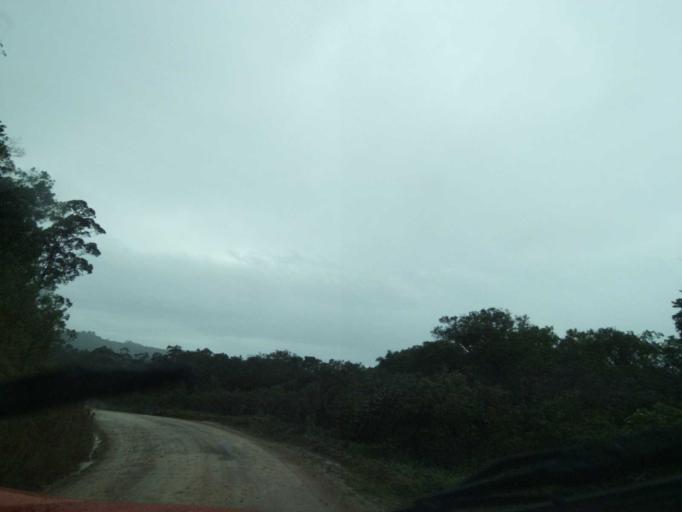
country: BR
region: Santa Catarina
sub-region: Anitapolis
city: Anitapolis
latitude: -27.9231
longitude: -49.1793
